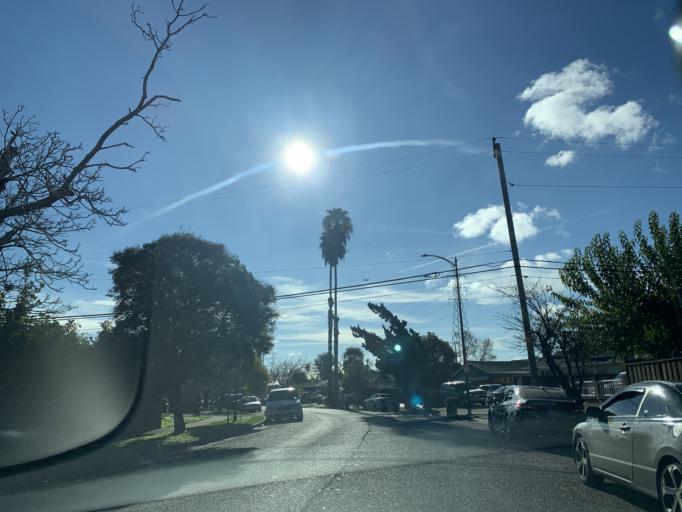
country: US
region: California
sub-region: Santa Clara County
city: Alum Rock
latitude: 37.3526
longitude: -121.8319
